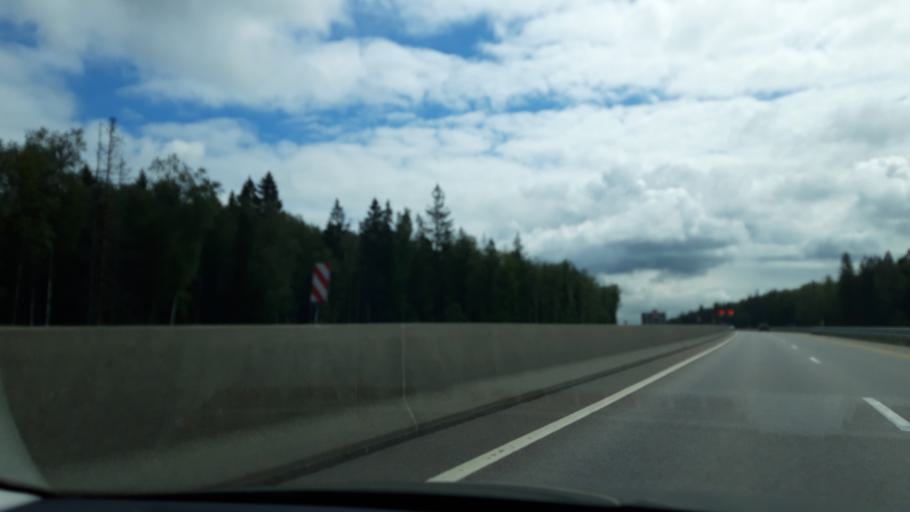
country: RU
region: Moskovskaya
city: Mendeleyevo
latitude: 56.0736
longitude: 37.2163
